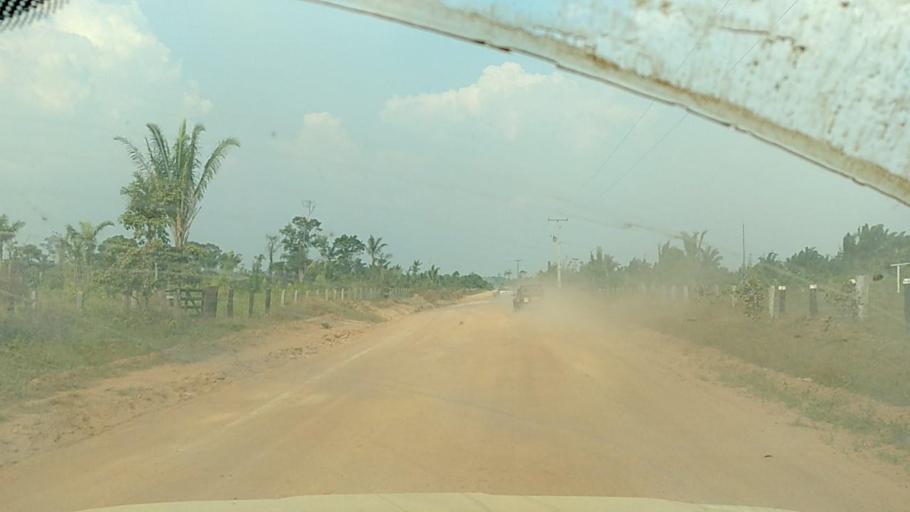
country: BR
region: Rondonia
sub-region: Porto Velho
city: Porto Velho
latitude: -8.6832
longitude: -63.1963
